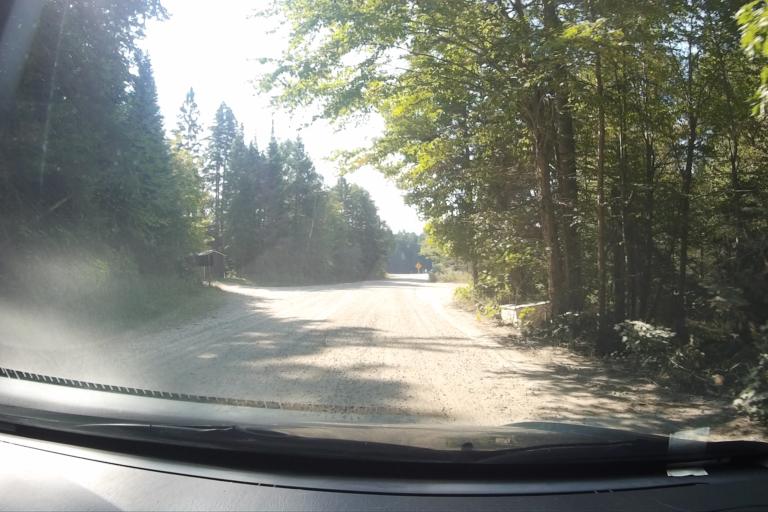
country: CA
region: Ontario
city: Huntsville
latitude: 45.5435
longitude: -78.6961
